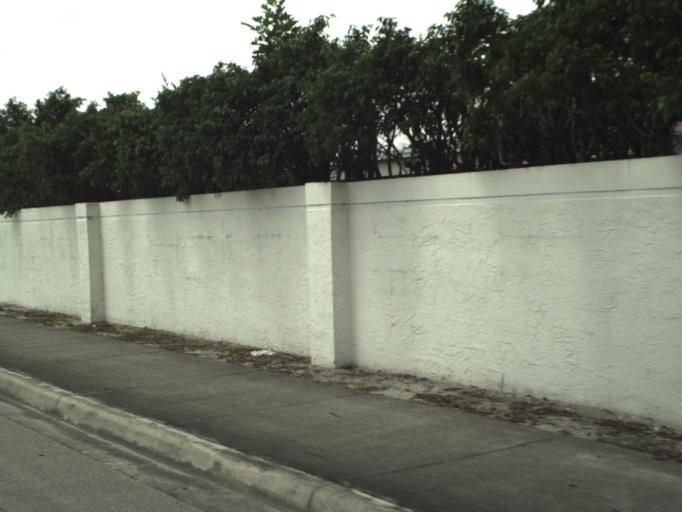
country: US
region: Florida
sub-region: Palm Beach County
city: Boynton Beach
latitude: 26.5030
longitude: -80.0902
